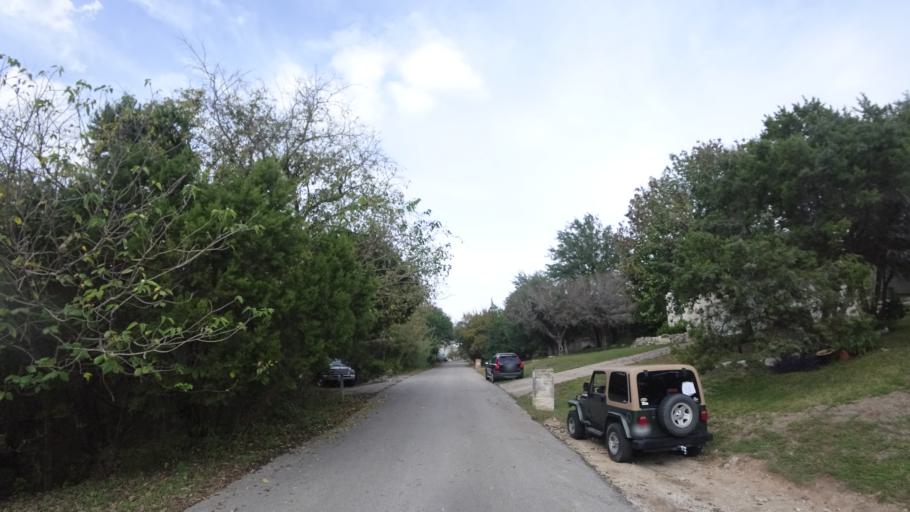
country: US
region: Texas
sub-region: Travis County
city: Hudson Bend
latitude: 30.3817
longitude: -97.9187
